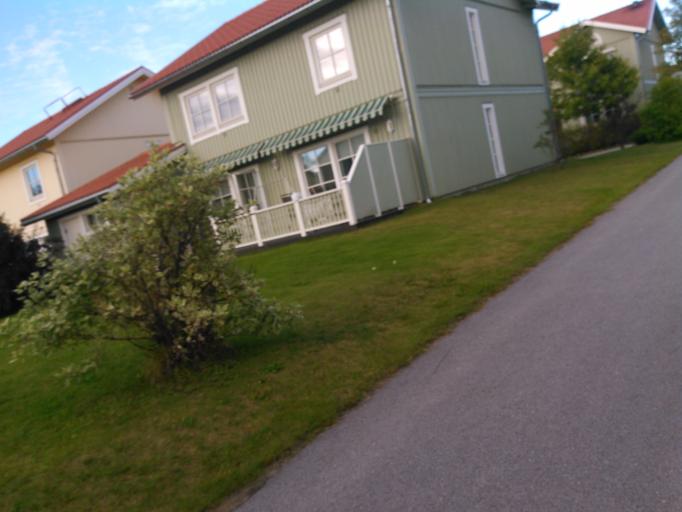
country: SE
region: Vaesterbotten
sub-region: Umea Kommun
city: Ersmark
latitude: 63.8058
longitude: 20.3403
